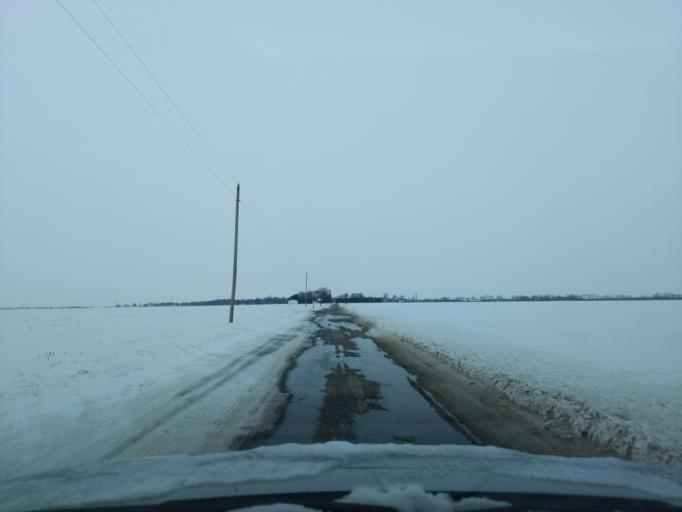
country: US
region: Indiana
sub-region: Benton County
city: Otterbein
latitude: 40.4675
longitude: -87.0927
